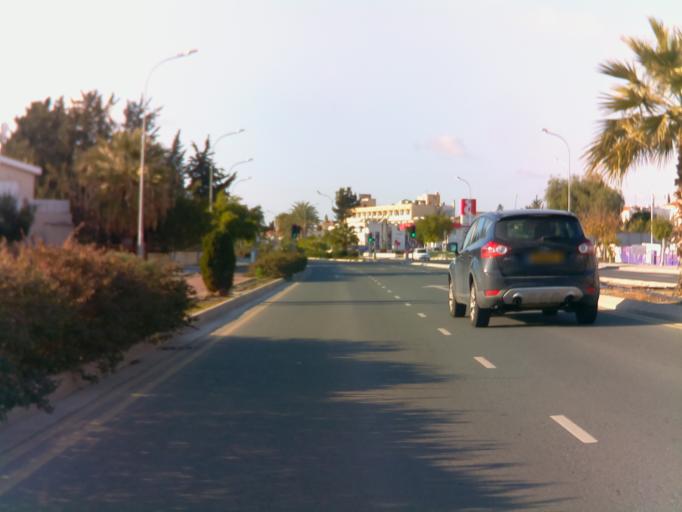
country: CY
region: Pafos
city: Paphos
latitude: 34.7589
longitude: 32.4231
